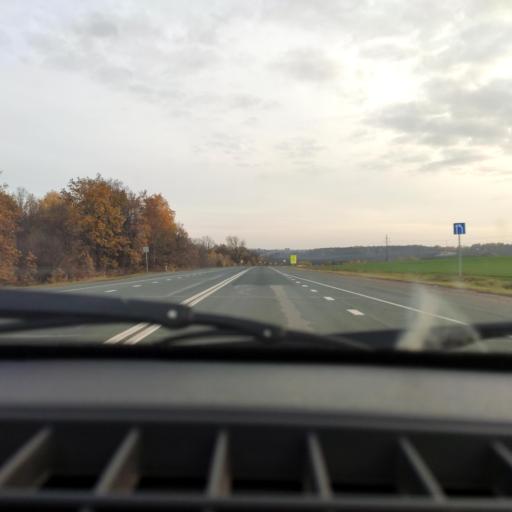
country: RU
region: Bashkortostan
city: Avdon
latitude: 54.7399
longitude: 55.7831
